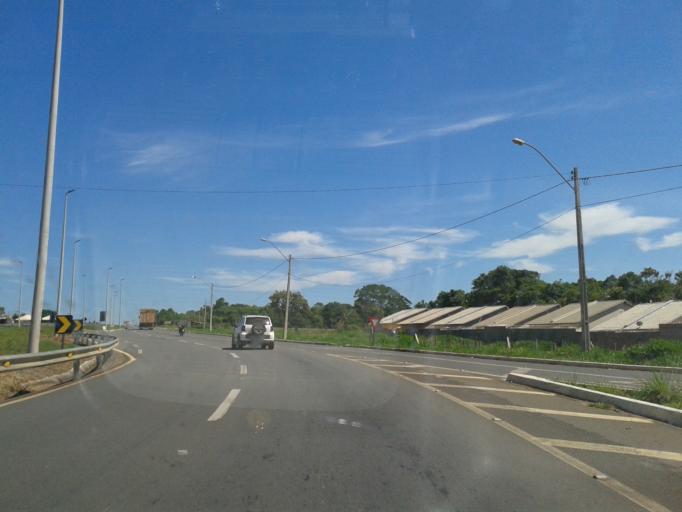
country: BR
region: Goias
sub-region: Bela Vista De Goias
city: Bela Vista de Goias
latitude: -16.9550
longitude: -48.9620
